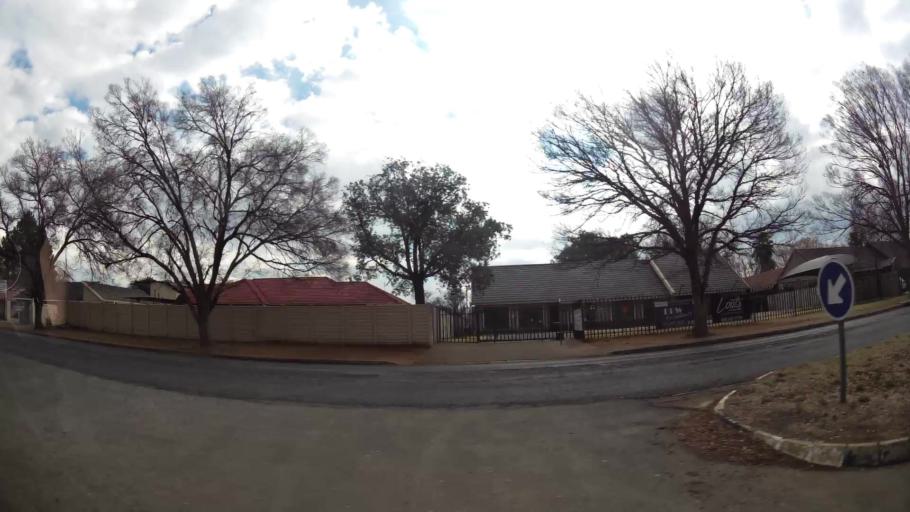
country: ZA
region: Gauteng
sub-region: Sedibeng District Municipality
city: Vereeniging
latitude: -26.6574
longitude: 27.9920
